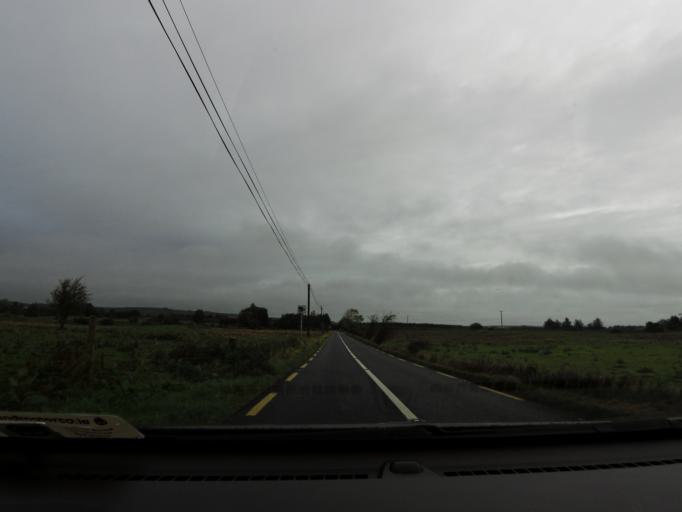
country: IE
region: Connaught
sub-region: Maigh Eo
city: Ballyhaunis
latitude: 53.6224
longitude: -8.7425
